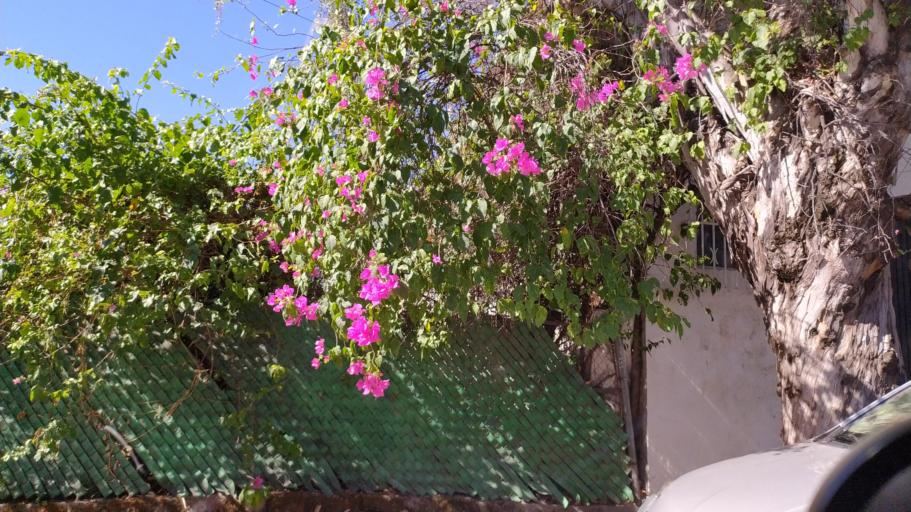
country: MX
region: Jalisco
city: Guadalajara
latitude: 20.6723
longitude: -103.4497
